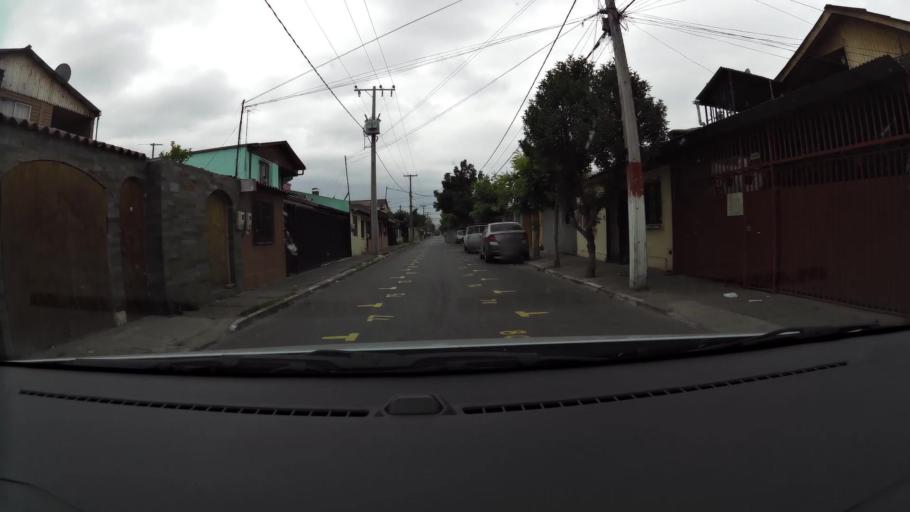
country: CL
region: Santiago Metropolitan
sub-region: Provincia de Santiago
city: Santiago
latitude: -33.5122
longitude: -70.6908
